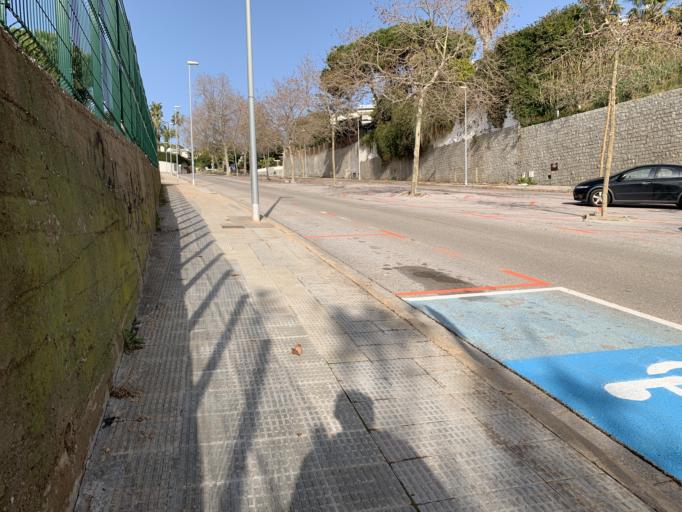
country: ES
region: Catalonia
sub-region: Provincia de Barcelona
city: El Masnou
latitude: 41.4748
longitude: 2.3008
